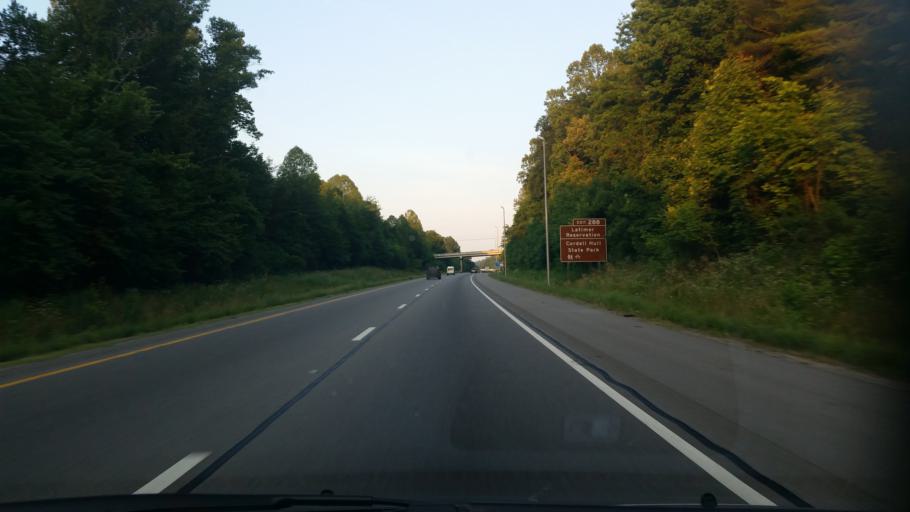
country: US
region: Tennessee
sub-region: Putnam County
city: Cookeville
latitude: 36.1355
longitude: -85.4911
